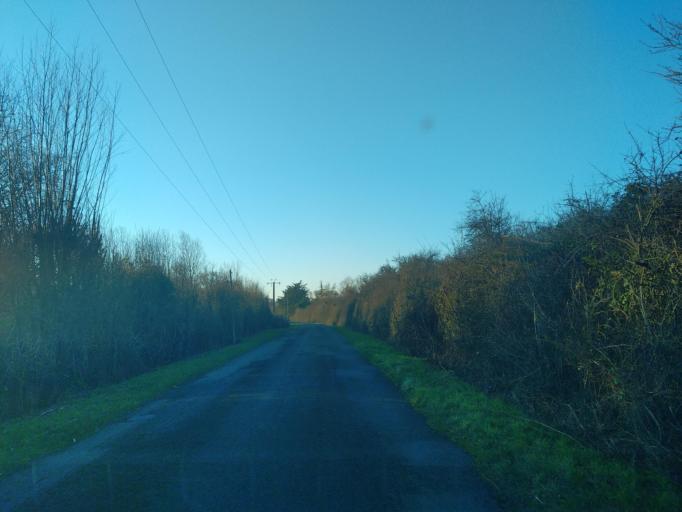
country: FR
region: Pays de la Loire
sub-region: Departement de la Vendee
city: Triaize
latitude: 46.3911
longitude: -1.2844
